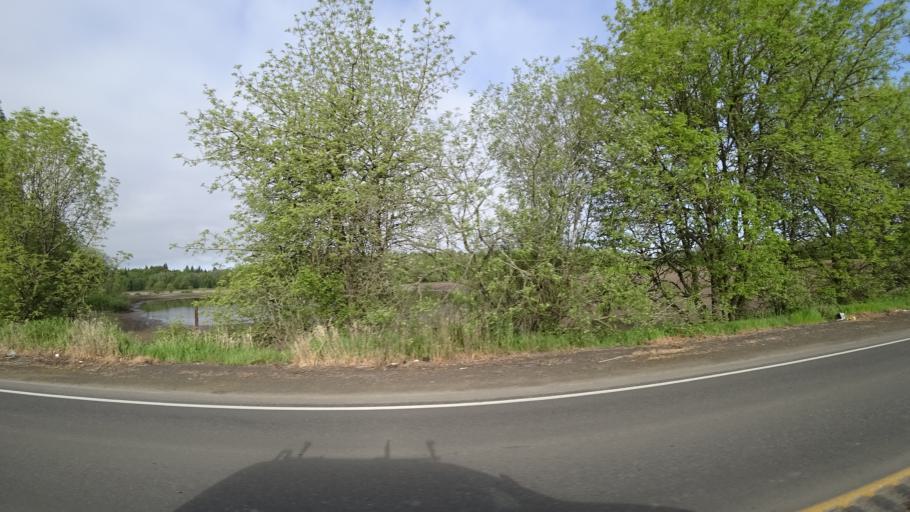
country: US
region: Oregon
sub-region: Washington County
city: Hillsboro
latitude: 45.4976
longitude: -122.9921
